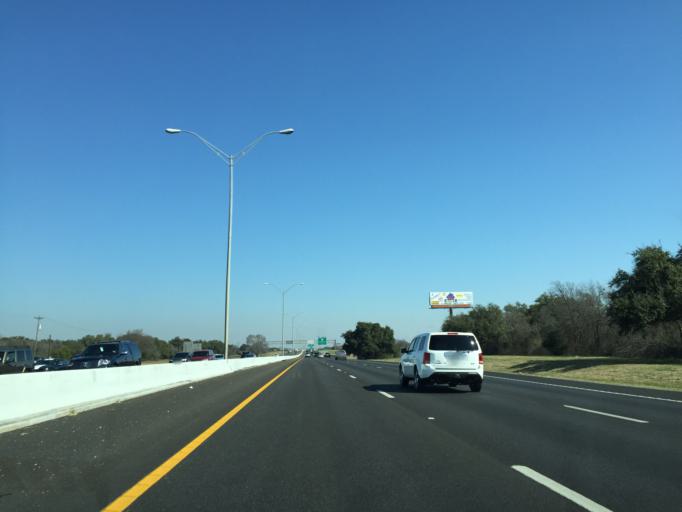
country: US
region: Texas
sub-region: Williamson County
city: Georgetown
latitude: 30.6562
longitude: -97.6754
